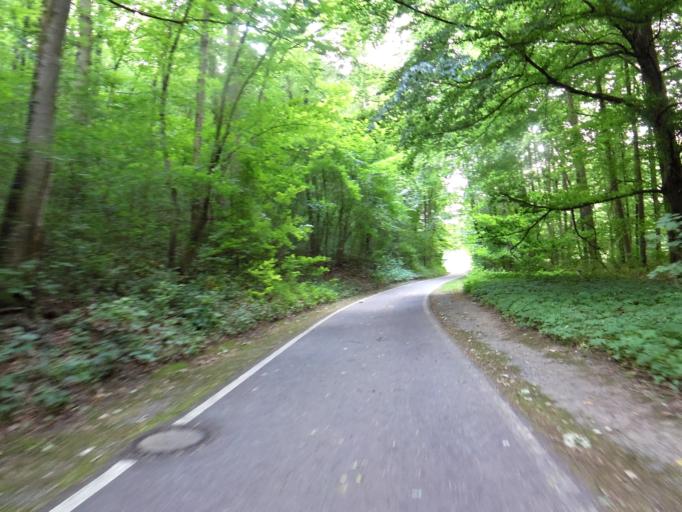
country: DE
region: Bavaria
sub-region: Regierungsbezirk Unterfranken
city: Reichenberg
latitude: 49.7394
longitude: 9.9485
